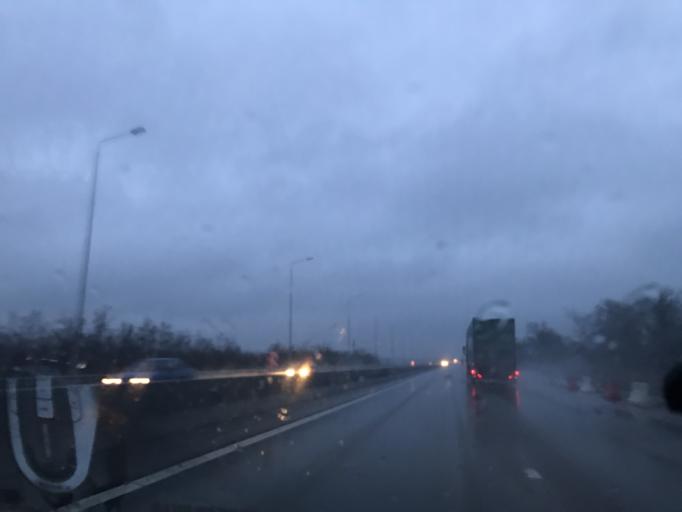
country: RU
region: Rostov
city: Samarskoye
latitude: 46.9405
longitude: 39.7113
